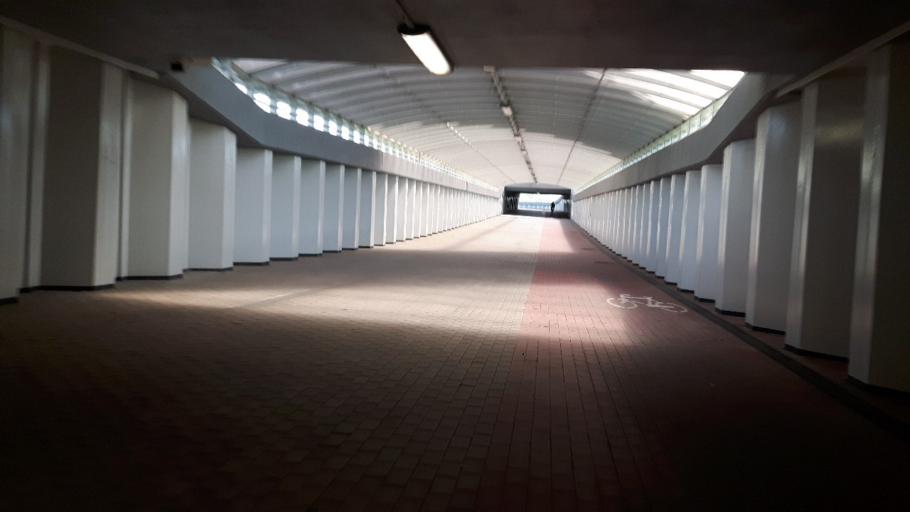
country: PL
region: Pomeranian Voivodeship
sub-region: Gdansk
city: Gdansk
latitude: 54.3489
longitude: 18.6968
